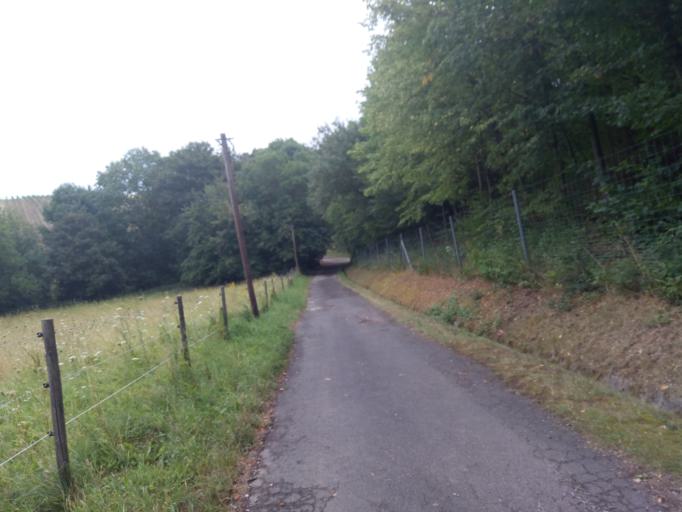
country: DE
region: Rheinland-Pfalz
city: Waldlaubersheim
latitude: 49.9239
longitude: 7.8327
